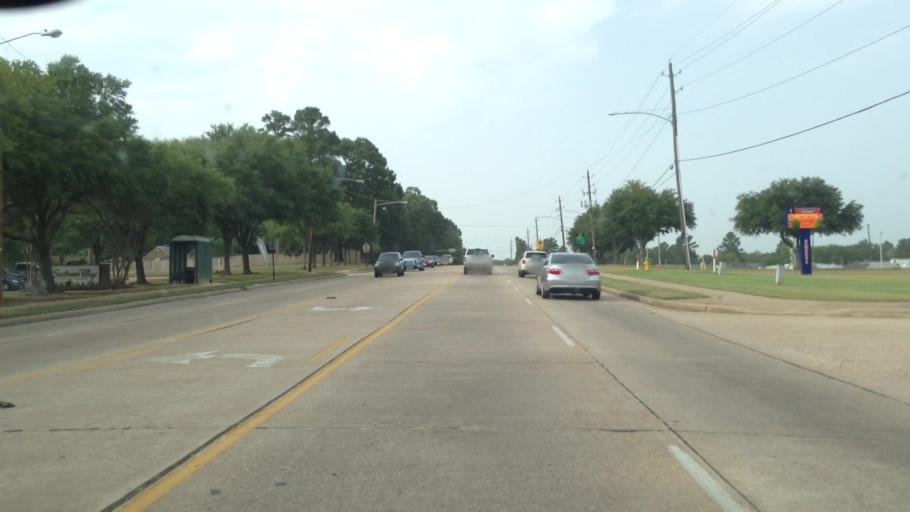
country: US
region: Louisiana
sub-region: De Soto Parish
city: Stonewall
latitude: 32.4092
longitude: -93.8147
